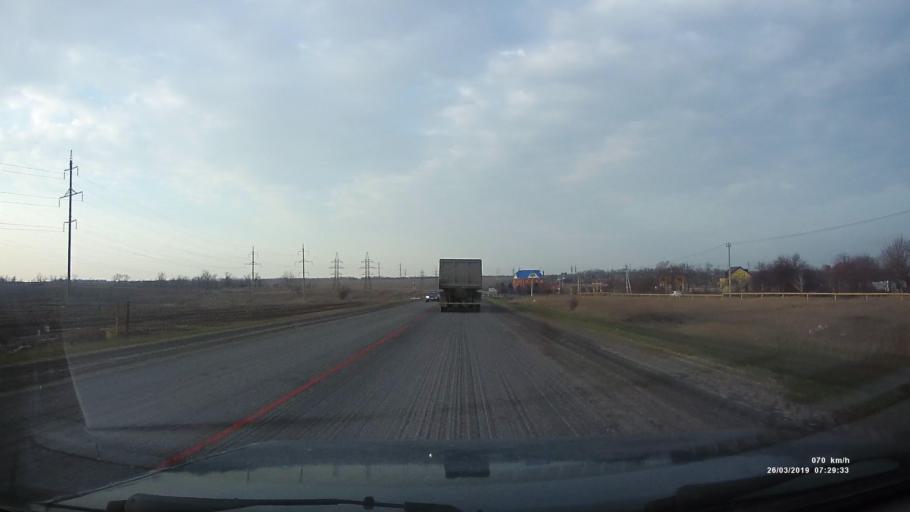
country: RU
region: Rostov
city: Novobessergenovka
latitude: 47.2442
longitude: 38.8159
